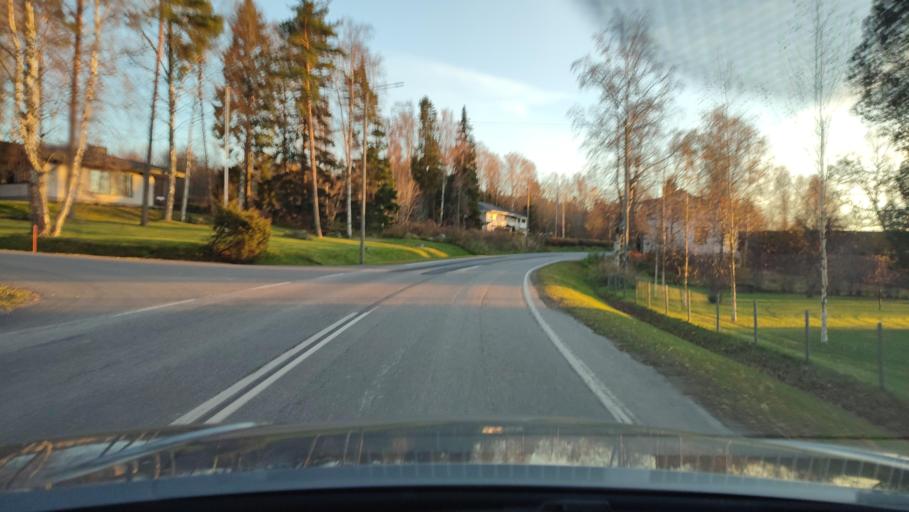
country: FI
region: Ostrobothnia
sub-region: Sydosterbotten
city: Naerpes
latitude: 62.4313
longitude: 21.3479
